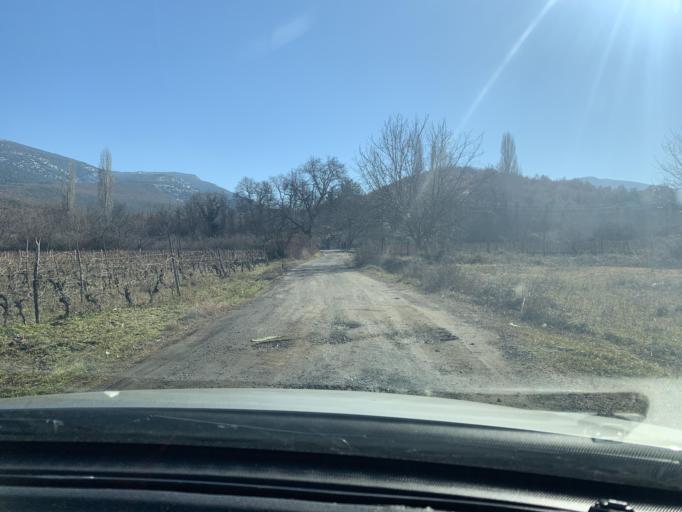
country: MK
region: Demir Kapija
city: Demir Kapija
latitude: 41.3902
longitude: 22.2249
